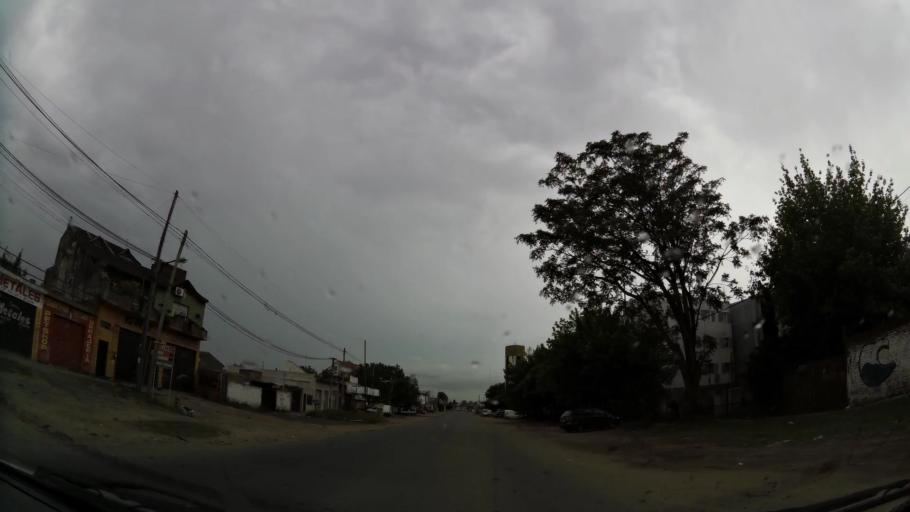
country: AR
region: Buenos Aires
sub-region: Partido de Quilmes
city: Quilmes
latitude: -34.7877
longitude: -58.2498
